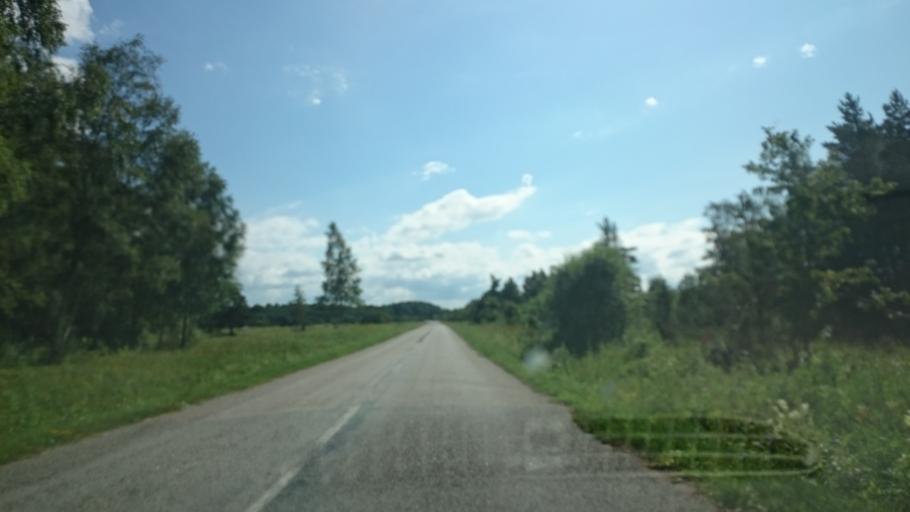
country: EE
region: Saare
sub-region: Orissaare vald
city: Orissaare
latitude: 58.5777
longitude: 22.7639
